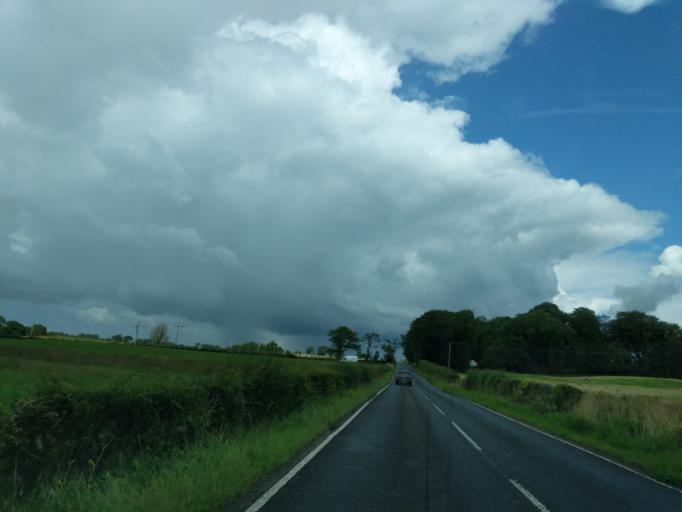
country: GB
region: Scotland
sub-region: East Ayrshire
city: Stewarton
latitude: 55.7118
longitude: -4.5170
